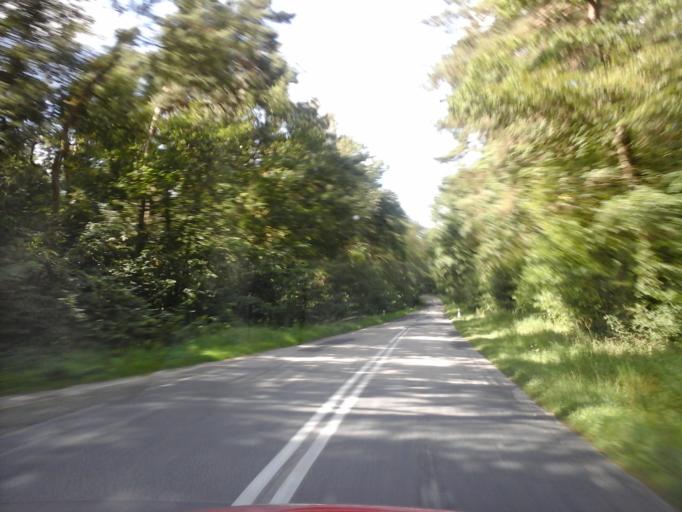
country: PL
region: West Pomeranian Voivodeship
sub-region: Powiat stargardzki
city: Dolice
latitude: 53.2029
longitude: 15.2779
